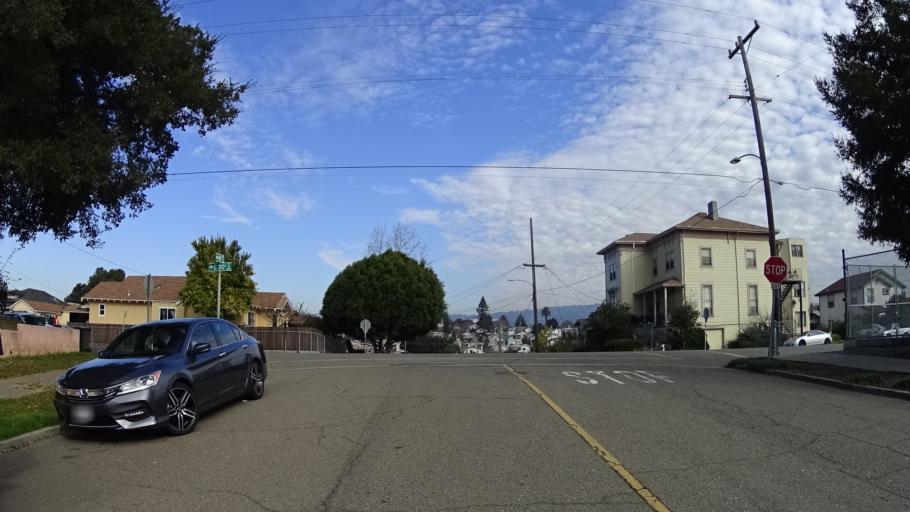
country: US
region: California
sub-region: Alameda County
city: Alameda
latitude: 37.7911
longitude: -122.2383
